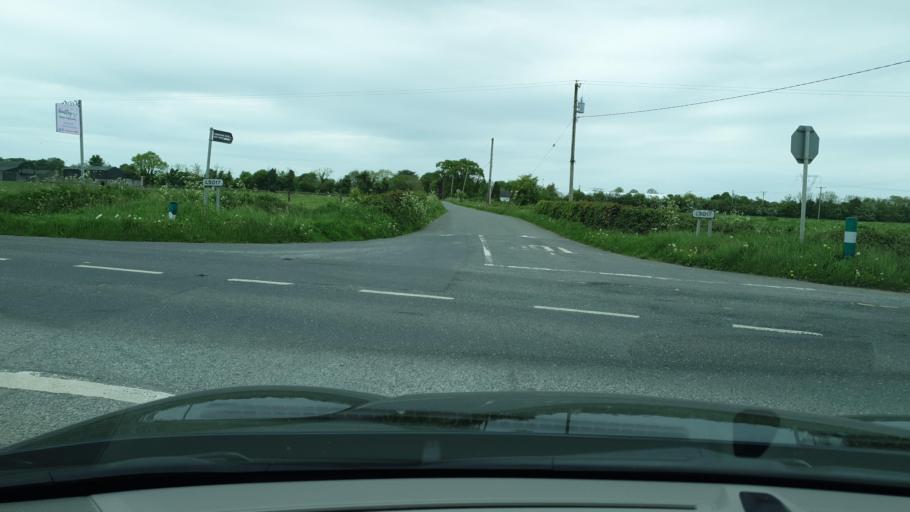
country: IE
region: Leinster
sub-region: An Mhi
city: Ratoath
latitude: 53.5143
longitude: -6.4860
